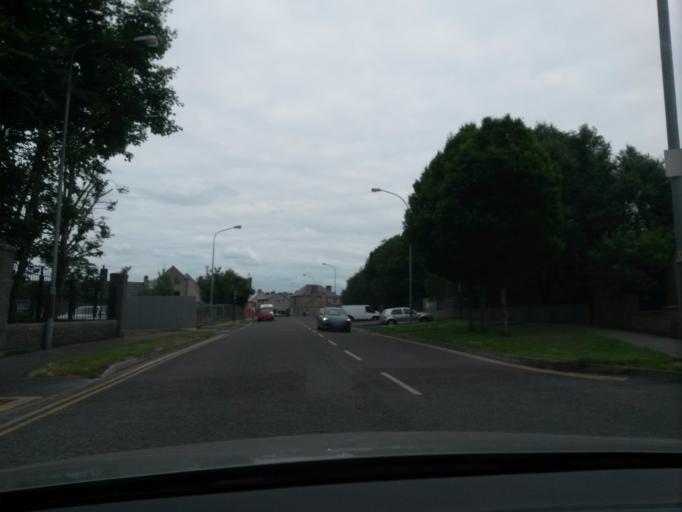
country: IE
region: Munster
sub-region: An Clar
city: Ennis
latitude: 52.8422
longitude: -8.9892
